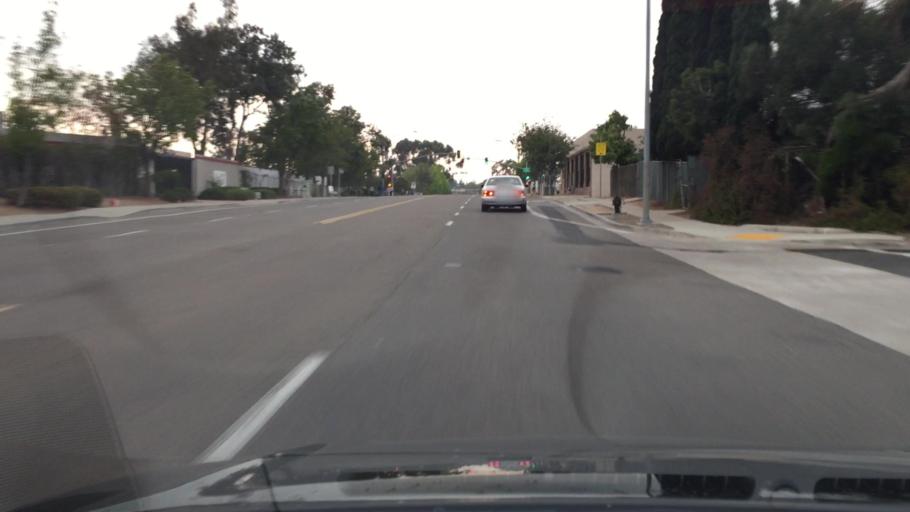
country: US
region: California
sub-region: San Diego County
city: National City
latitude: 32.7201
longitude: -117.0935
